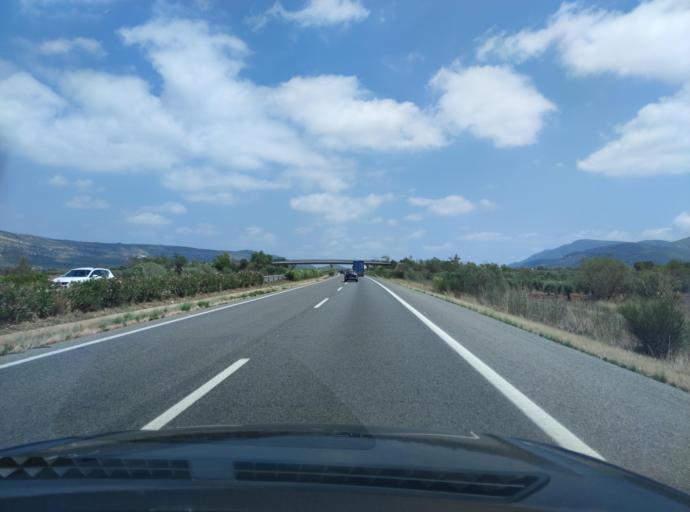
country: ES
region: Catalonia
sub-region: Provincia de Tarragona
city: Ulldecona
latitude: 40.5977
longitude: 0.4707
